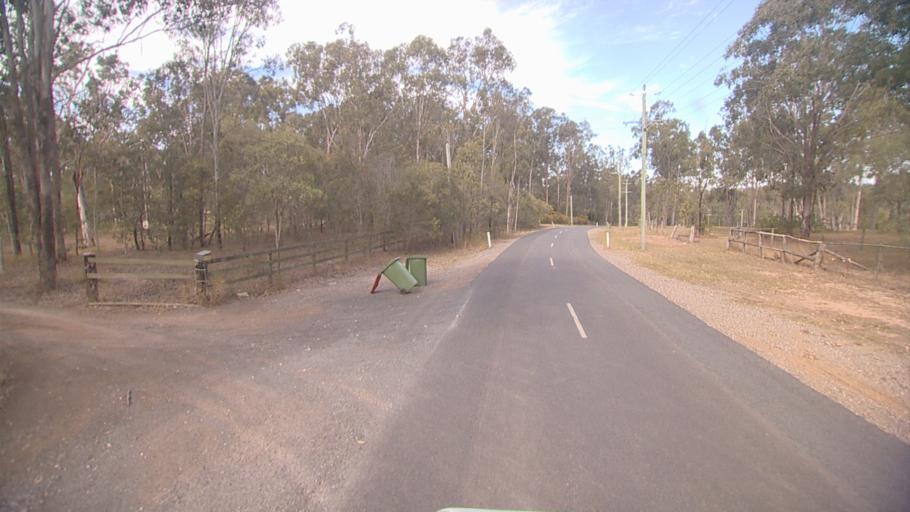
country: AU
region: Queensland
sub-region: Logan
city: North Maclean
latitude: -27.7542
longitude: 152.9744
